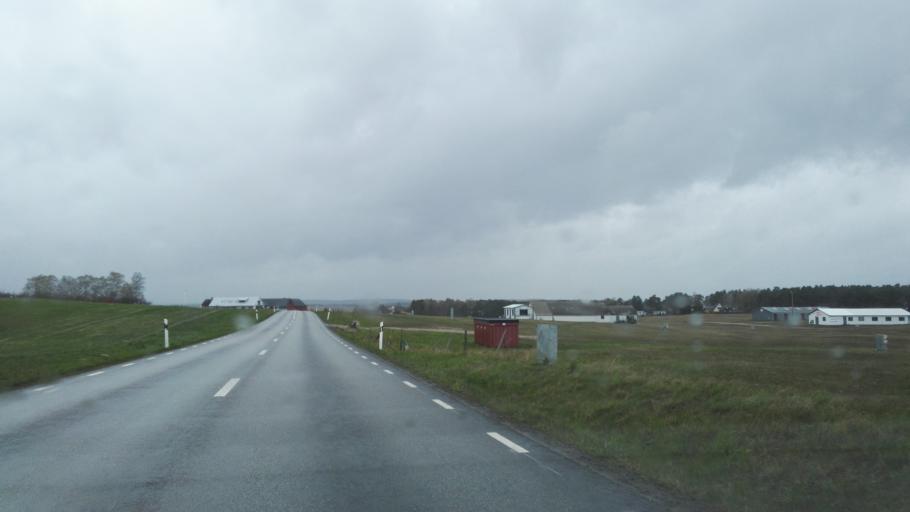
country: SE
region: Skane
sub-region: Simrishamns Kommun
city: Kivik
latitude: 55.6916
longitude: 14.2099
